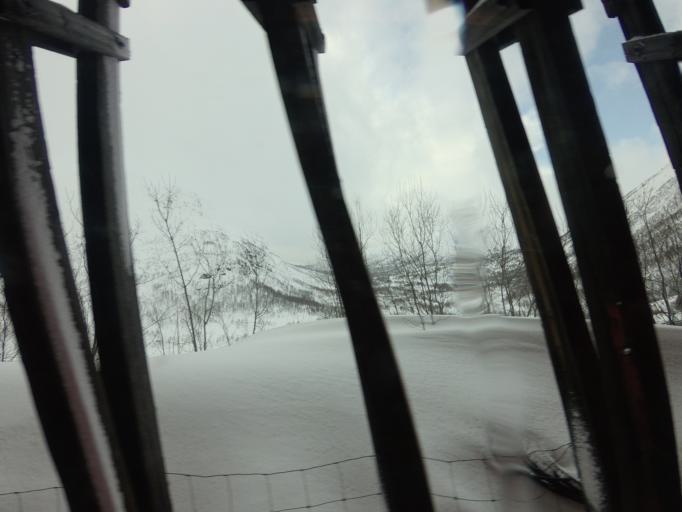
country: NO
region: Hordaland
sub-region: Ulvik
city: Ulvik
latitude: 60.7040
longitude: 6.9670
